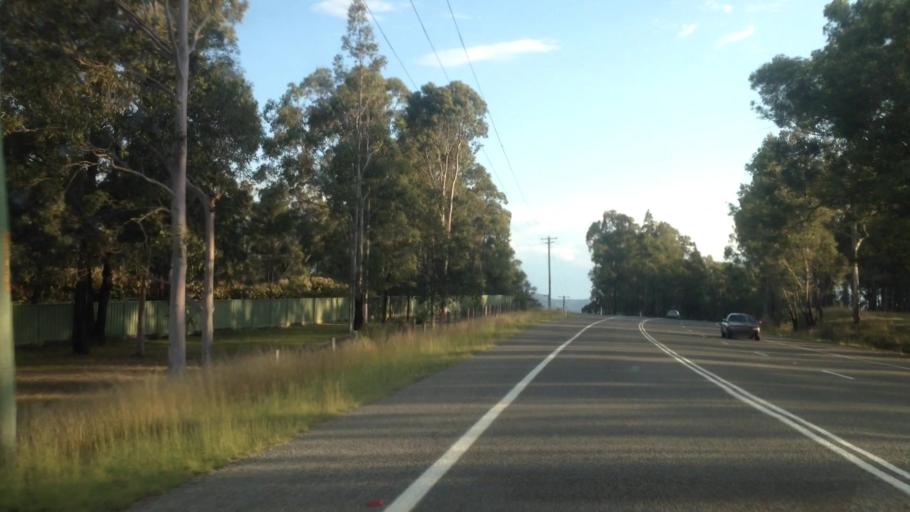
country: AU
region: New South Wales
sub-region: Cessnock
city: Kurri Kurri
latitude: -32.8593
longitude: 151.4842
